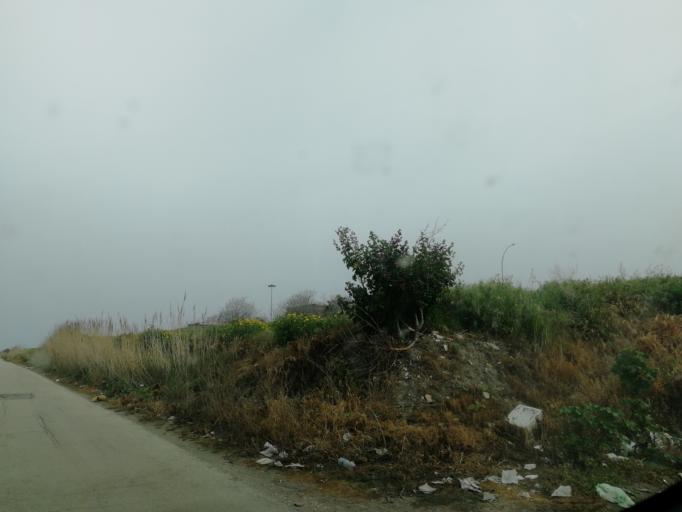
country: IT
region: Apulia
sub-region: Provincia di Barletta - Andria - Trani
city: Barletta
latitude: 41.3191
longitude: 16.3016
